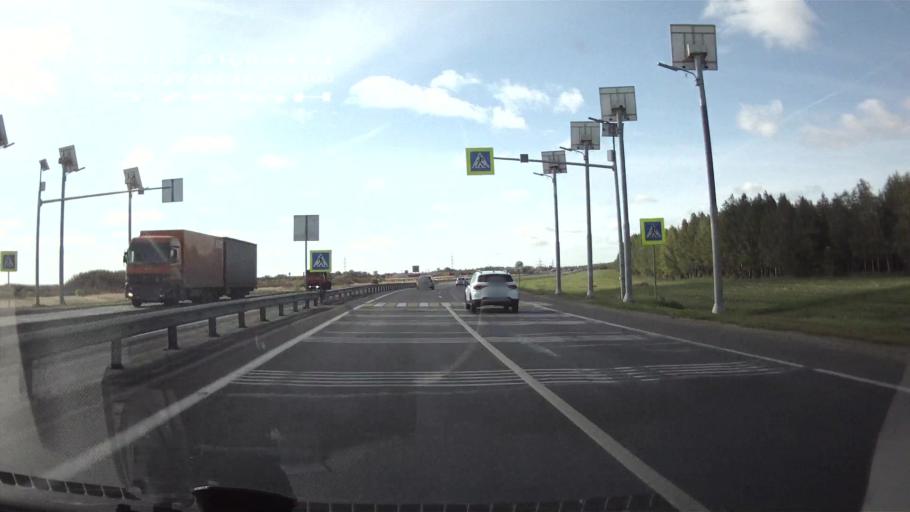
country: RU
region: Ulyanovsk
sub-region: Ulyanovskiy Rayon
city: Ulyanovsk
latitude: 54.2695
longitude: 48.2604
